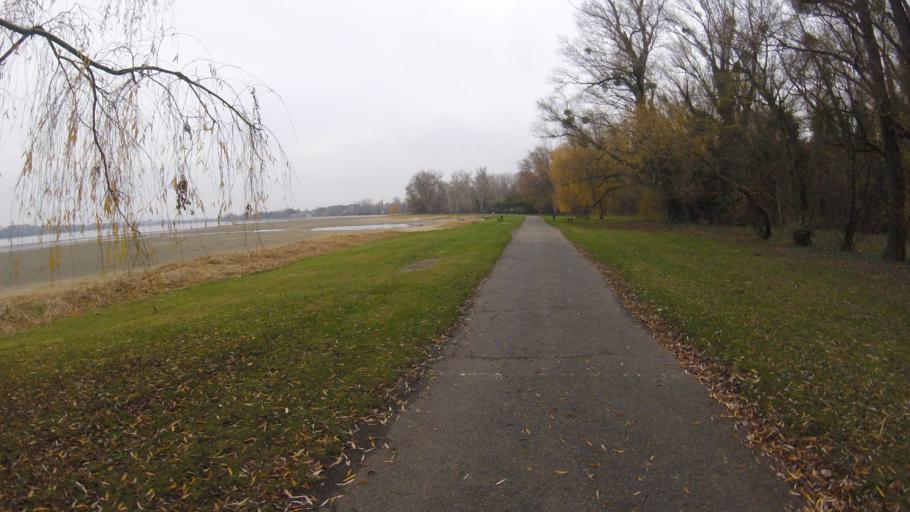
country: HU
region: Komarom-Esztergom
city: Tata
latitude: 47.6368
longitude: 18.3391
